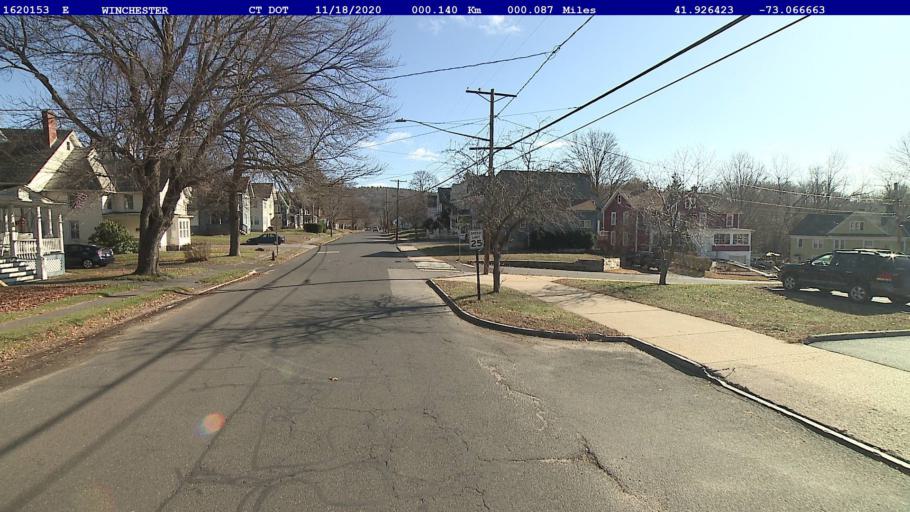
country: US
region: Connecticut
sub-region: Litchfield County
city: Winsted
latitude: 41.9264
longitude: -73.0667
